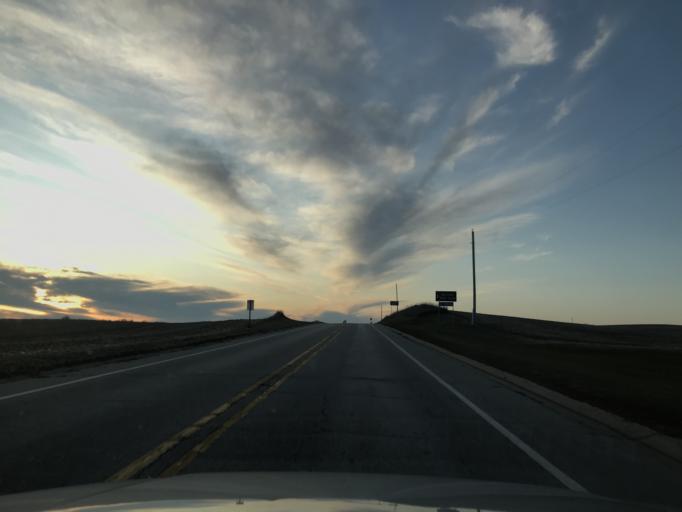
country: US
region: Illinois
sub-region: Henderson County
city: Oquawka
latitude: 41.0187
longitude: -90.8499
